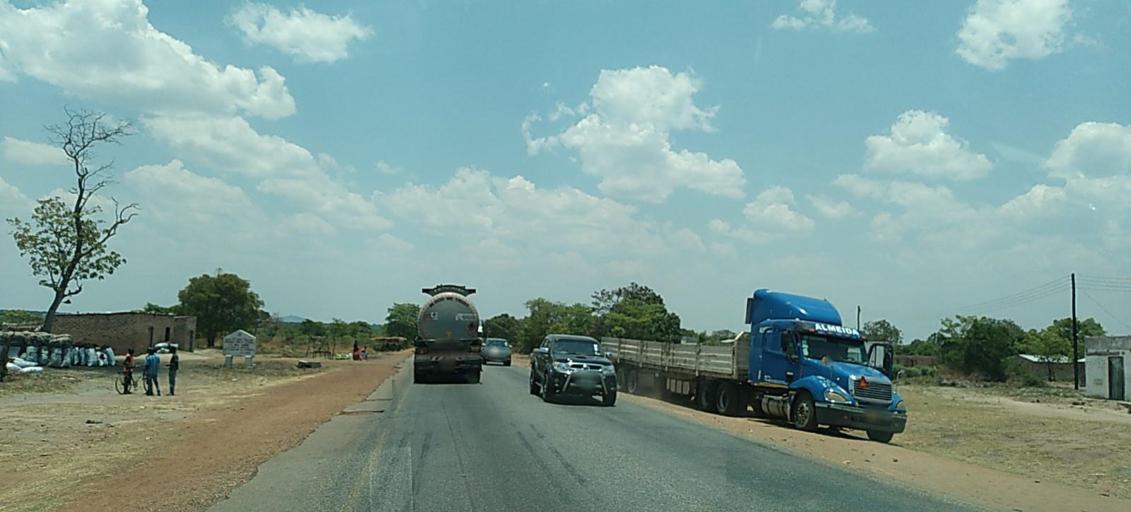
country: ZM
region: Central
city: Kapiri Mposhi
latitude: -13.7734
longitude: 28.6447
